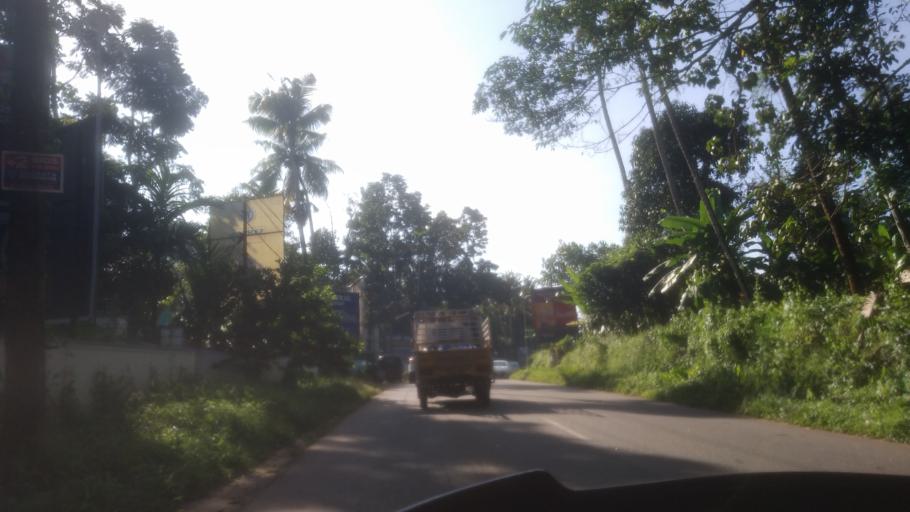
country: IN
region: Kerala
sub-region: Ernakulam
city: Muvattupuzha
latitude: 9.9763
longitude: 76.5297
